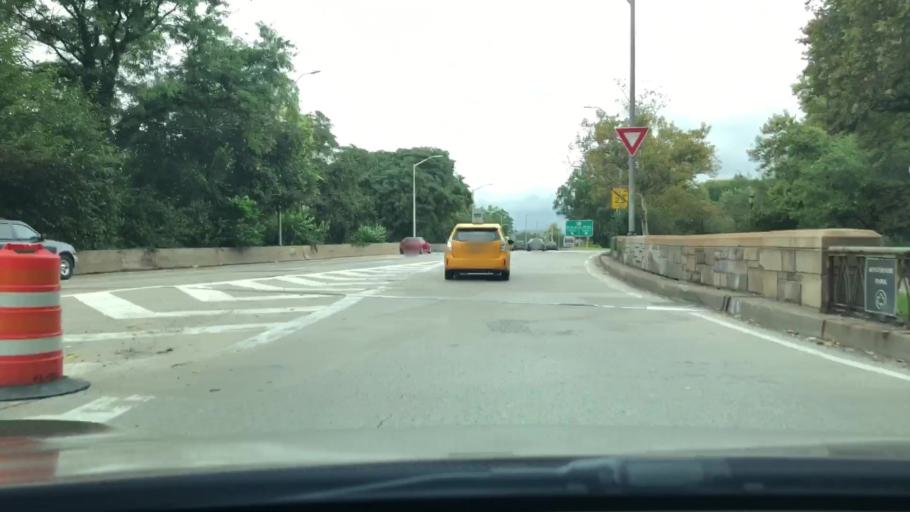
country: US
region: New York
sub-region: New York County
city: Manhattan
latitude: 40.7967
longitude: -73.9757
